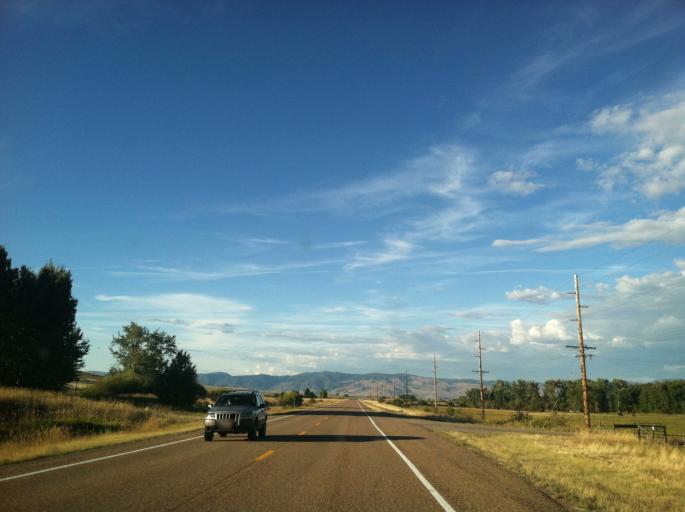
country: US
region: Montana
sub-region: Granite County
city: Philipsburg
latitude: 46.5431
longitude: -113.2202
